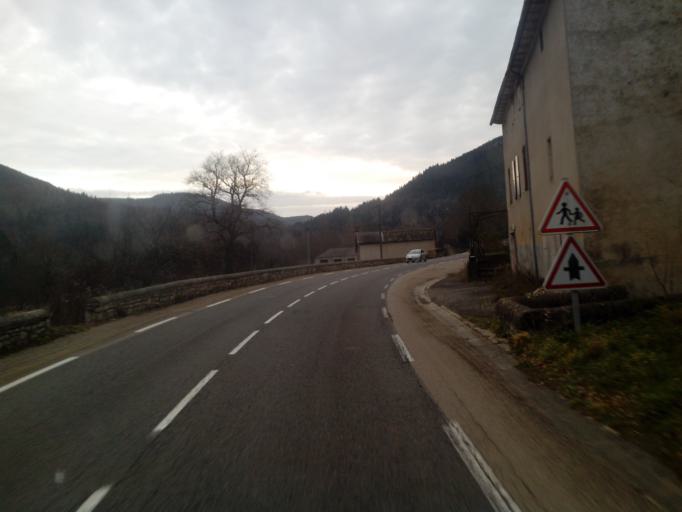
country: FR
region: Languedoc-Roussillon
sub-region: Departement de la Lozere
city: Florac
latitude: 44.3108
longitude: 3.5985
